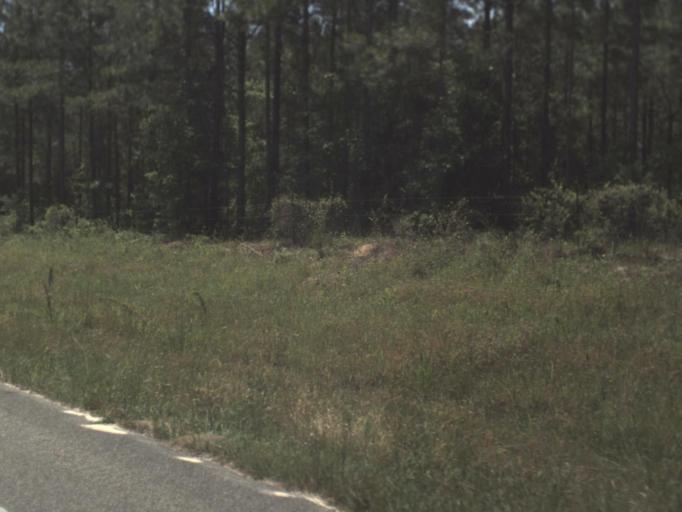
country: US
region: Florida
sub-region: Jackson County
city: Marianna
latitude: 30.6630
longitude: -85.2248
